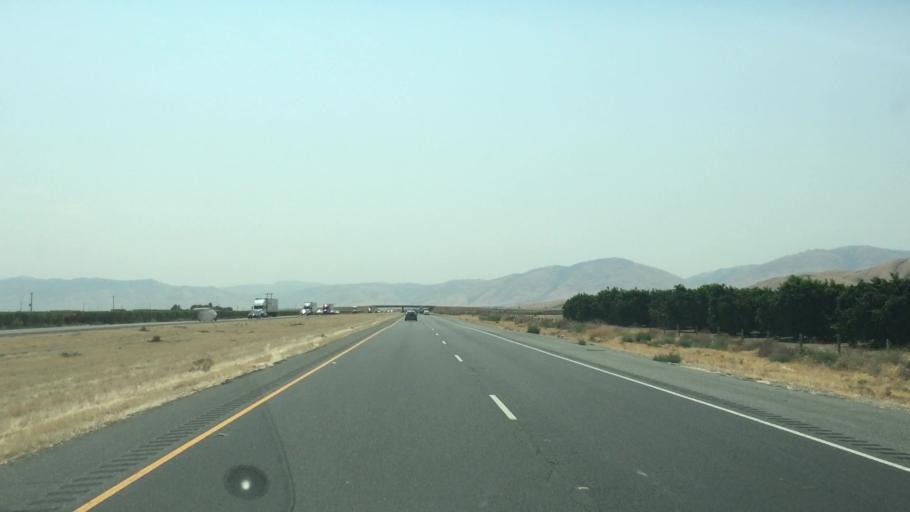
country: US
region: California
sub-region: Kern County
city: Weedpatch
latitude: 35.0442
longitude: -118.9844
